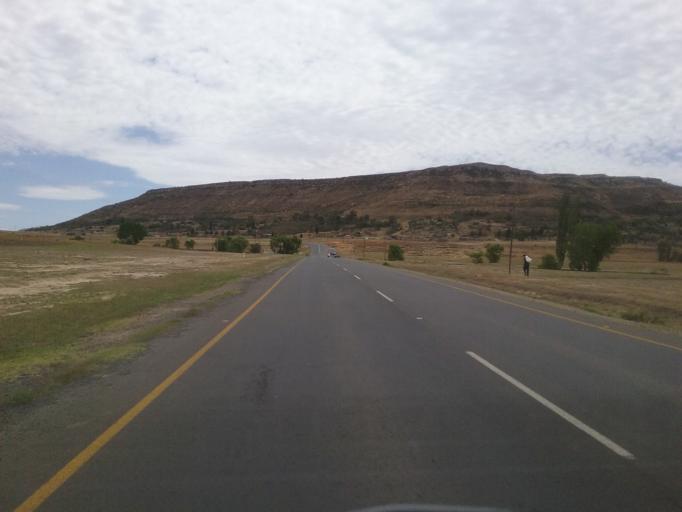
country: LS
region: Maseru
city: Nako
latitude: -29.6128
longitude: 27.5003
